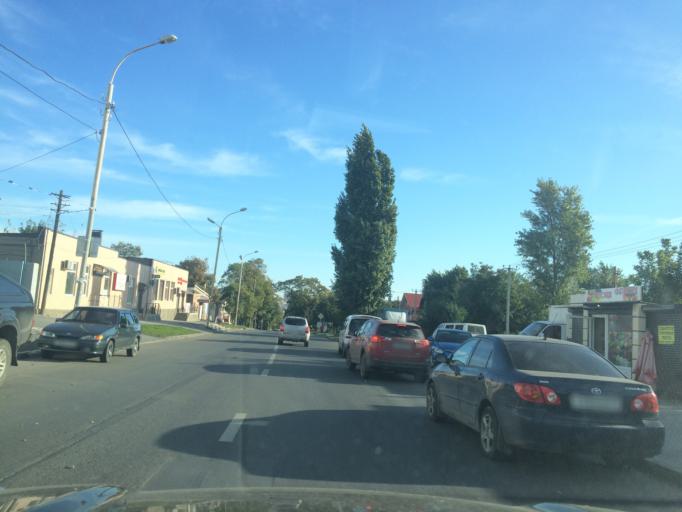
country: RU
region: Rostov
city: Rostov-na-Donu
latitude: 47.2087
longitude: 39.6902
